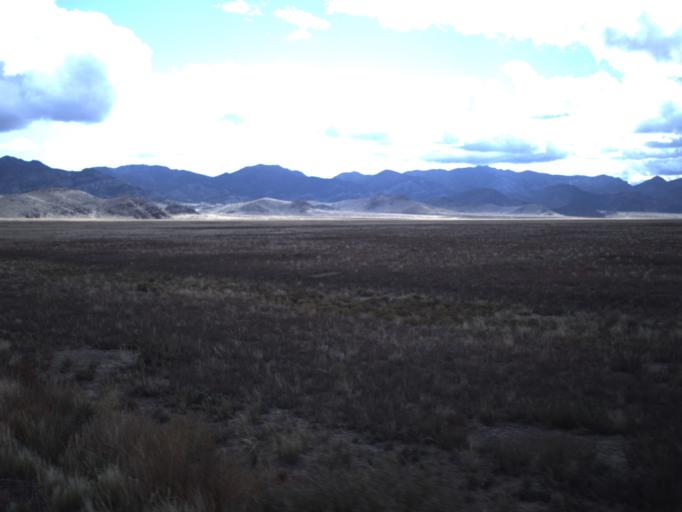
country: US
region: Utah
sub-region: Beaver County
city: Milford
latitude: 38.5186
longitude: -113.6449
